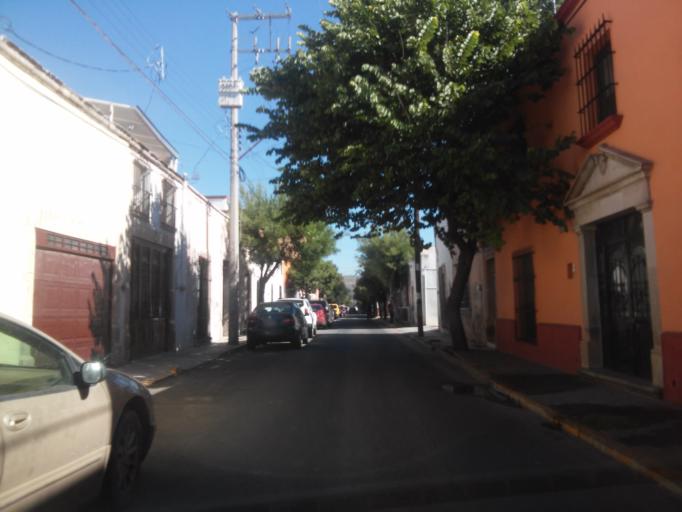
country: MX
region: Durango
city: Victoria de Durango
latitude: 24.0288
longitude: -104.6691
